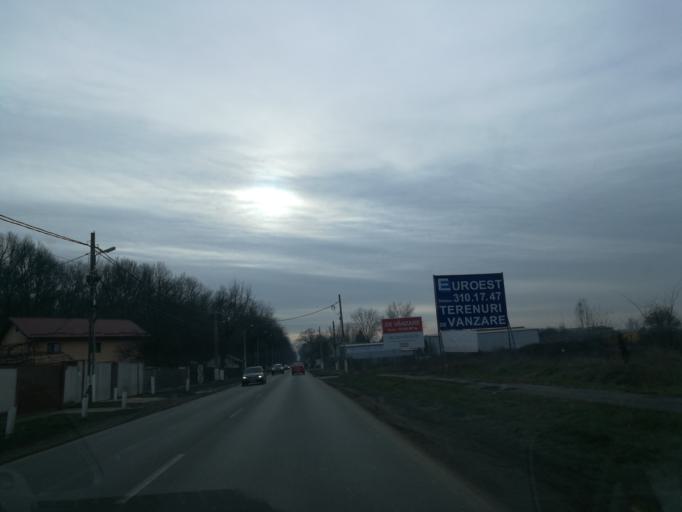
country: RO
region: Ilfov
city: Stefanestii de Jos
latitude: 44.5233
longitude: 26.1959
